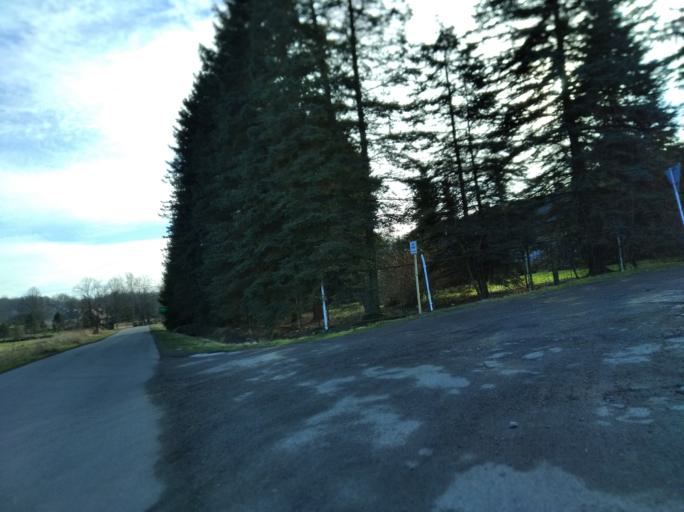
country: PL
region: Subcarpathian Voivodeship
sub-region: Powiat strzyzowski
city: Konieczkowa
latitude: 49.8241
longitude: 21.9259
